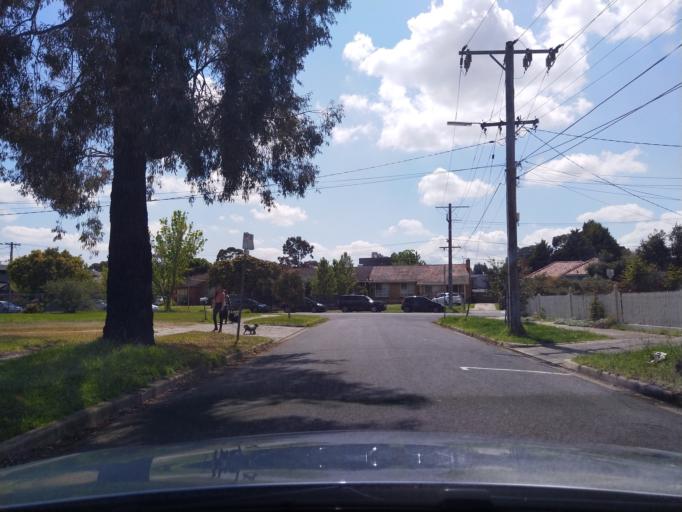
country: AU
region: Victoria
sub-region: Banyule
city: Bellfield
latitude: -37.7523
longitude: 145.0447
